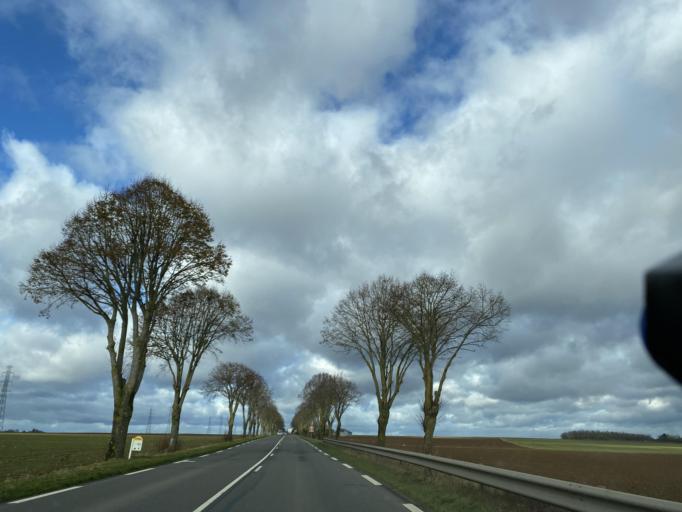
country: FR
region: Centre
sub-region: Departement d'Eure-et-Loir
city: Baigneaux
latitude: 48.1376
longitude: 1.8507
